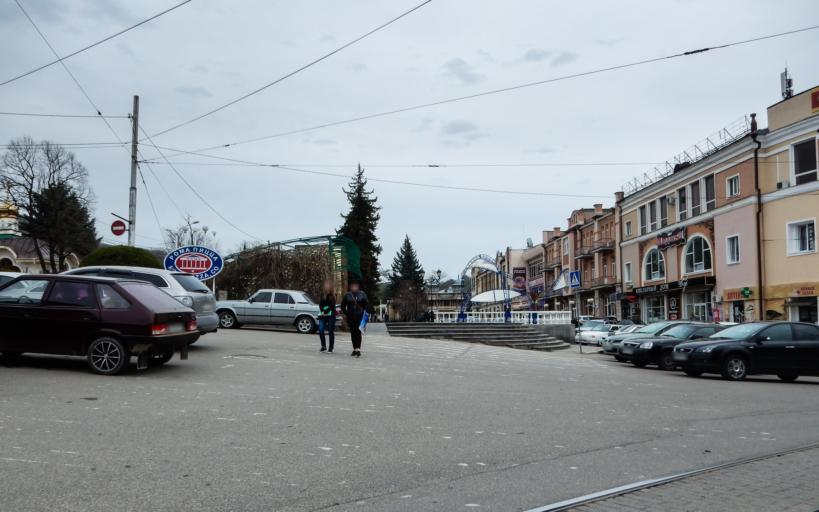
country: RU
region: Stavropol'skiy
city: Goryachevodskiy
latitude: 44.0365
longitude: 43.0781
